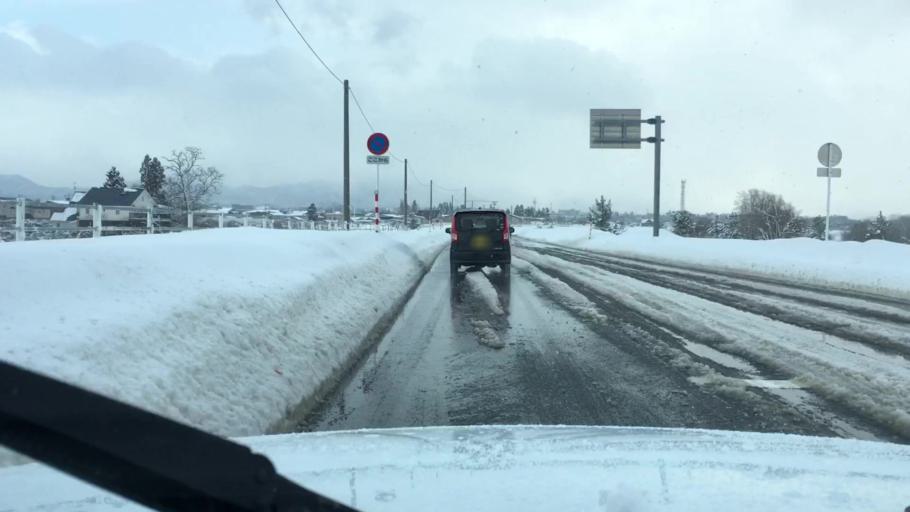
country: JP
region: Aomori
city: Hirosaki
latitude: 40.6277
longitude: 140.4743
